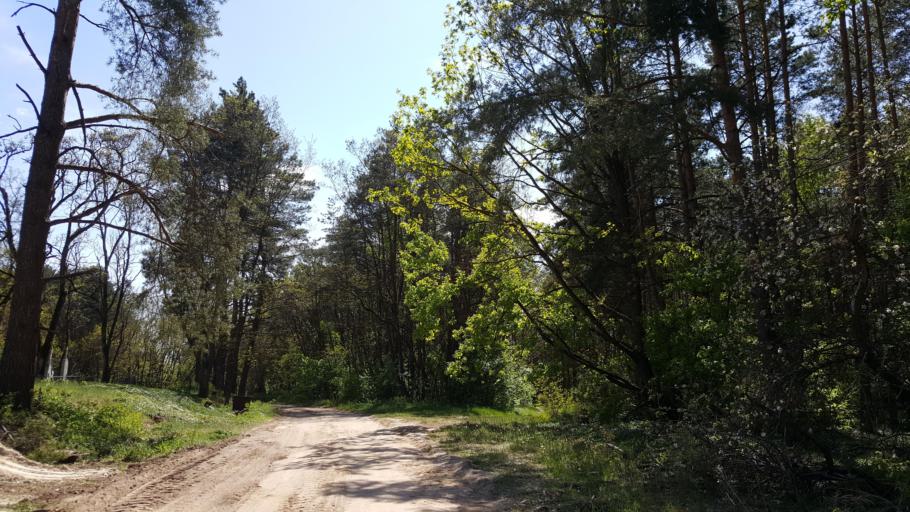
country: BY
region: Brest
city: Zhabinka
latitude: 52.3661
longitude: 24.1593
